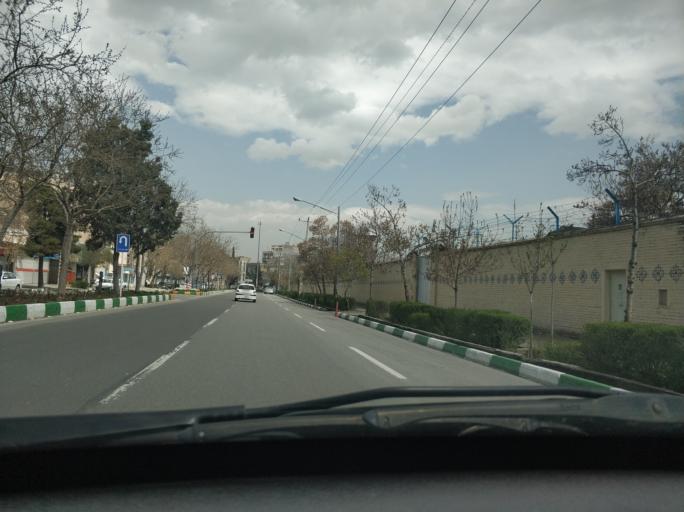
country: IR
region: Razavi Khorasan
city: Mashhad
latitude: 36.2829
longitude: 59.5778
